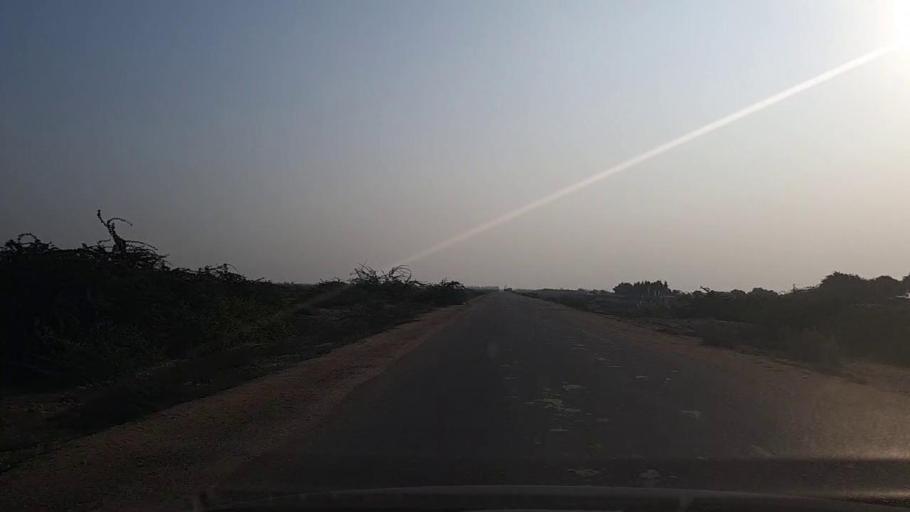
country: PK
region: Sindh
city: Mirpur Sakro
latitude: 24.4805
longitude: 67.8047
